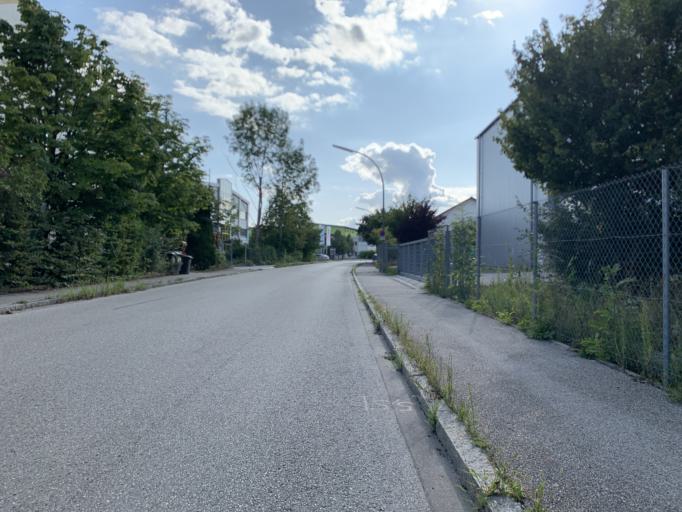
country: DE
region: Bavaria
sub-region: Upper Bavaria
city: Freising
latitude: 48.3888
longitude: 11.7609
